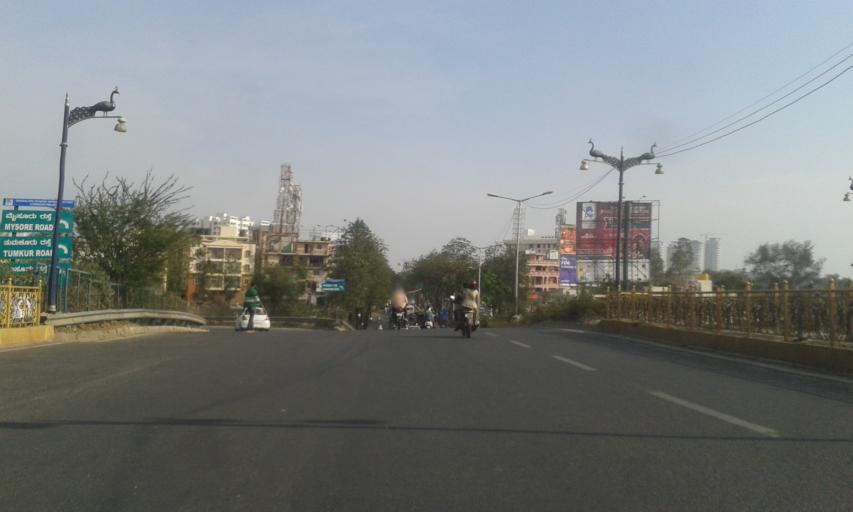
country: IN
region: Karnataka
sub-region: Bangalore Urban
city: Bangalore
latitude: 12.9398
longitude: 77.5326
